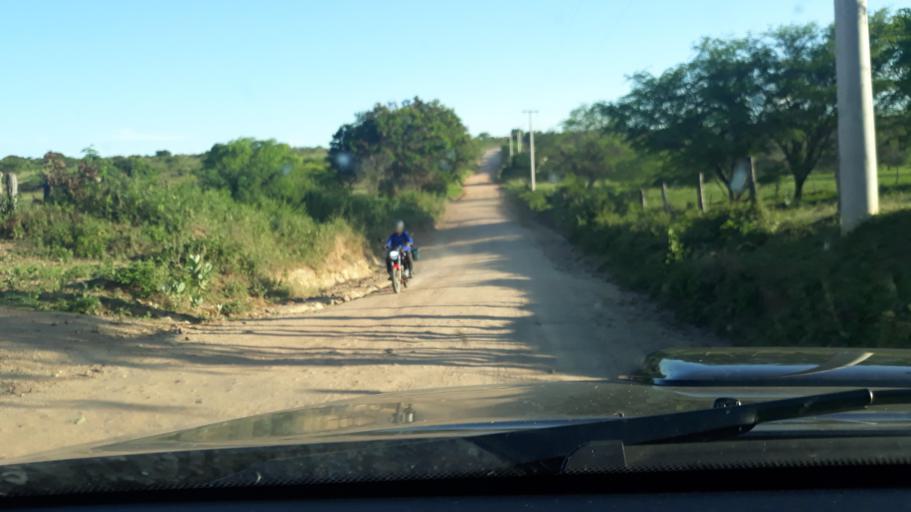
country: BR
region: Bahia
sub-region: Riacho De Santana
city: Riacho de Santana
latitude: -13.7878
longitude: -42.7129
